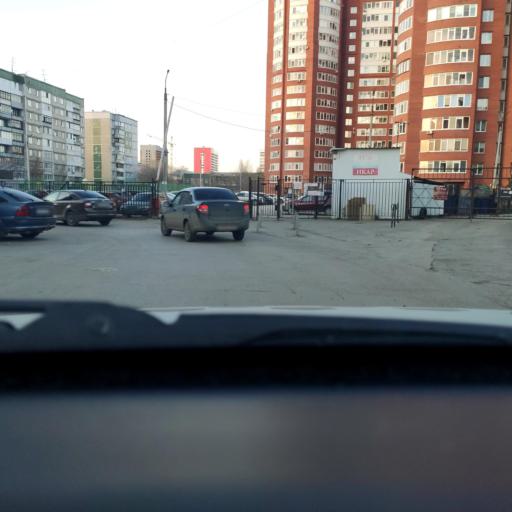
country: RU
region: Perm
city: Perm
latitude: 57.9635
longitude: 56.2369
